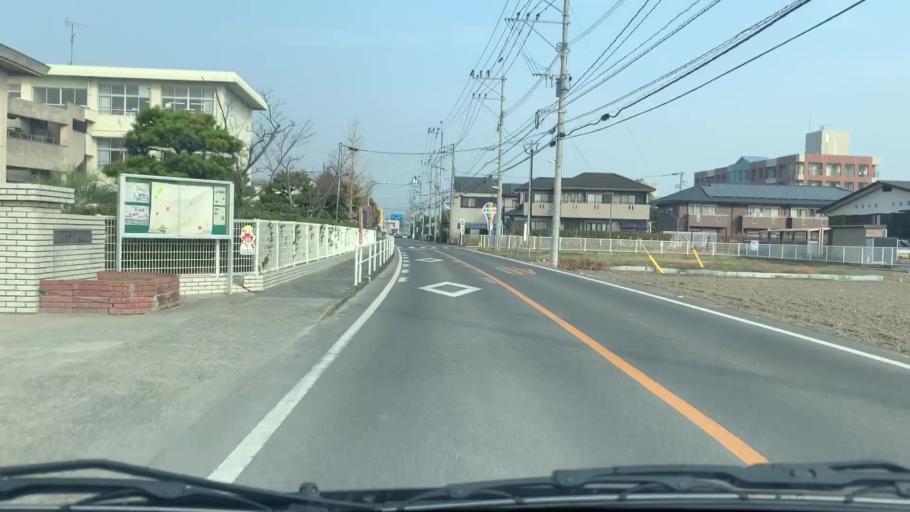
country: JP
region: Saga Prefecture
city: Saga-shi
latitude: 33.2406
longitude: 130.2584
